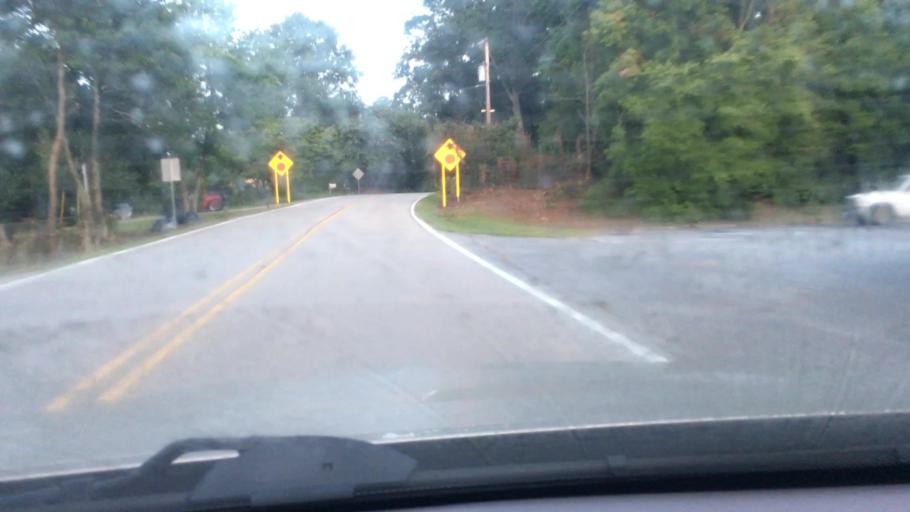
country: US
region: South Carolina
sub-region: Lexington County
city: Irmo
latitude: 34.1361
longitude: -81.1879
